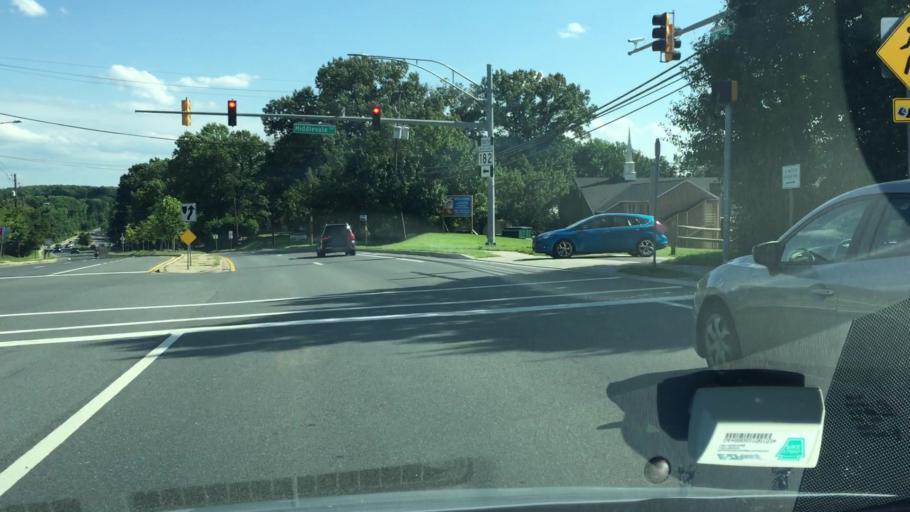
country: US
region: Maryland
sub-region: Montgomery County
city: Layhill
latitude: 39.0813
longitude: -77.0471
